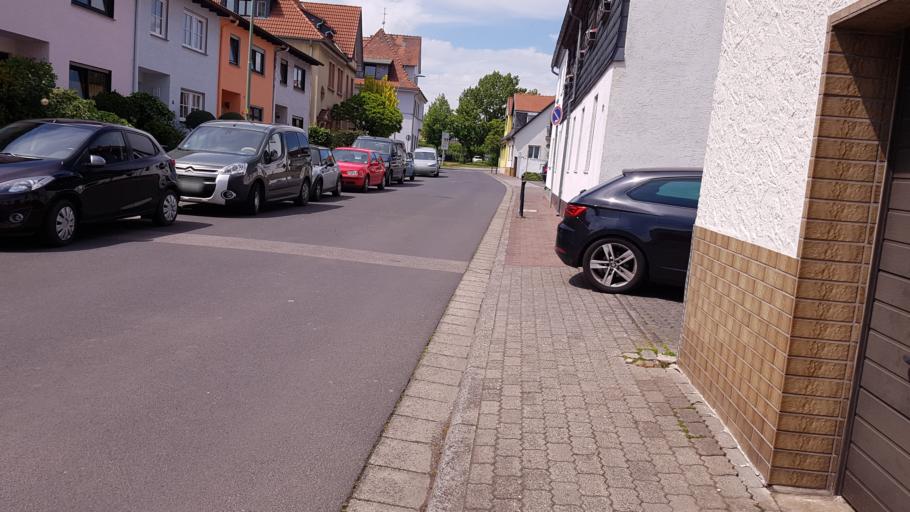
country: DE
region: Hesse
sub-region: Regierungsbezirk Darmstadt
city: Bad Vilbel
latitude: 50.1850
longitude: 8.7403
